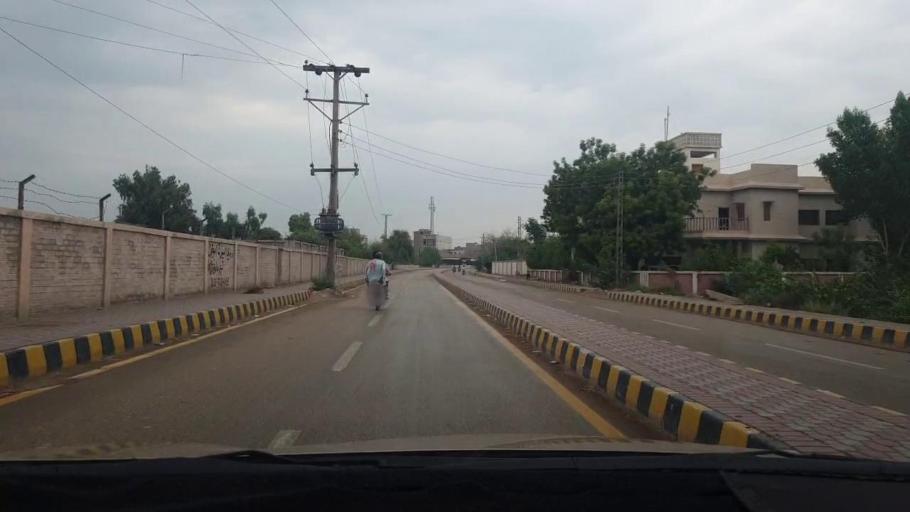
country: PK
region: Sindh
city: Larkana
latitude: 27.5645
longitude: 68.1975
